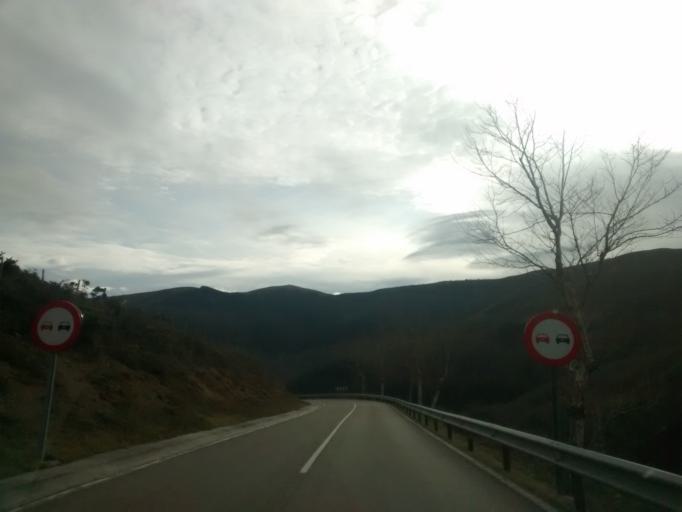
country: ES
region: Cantabria
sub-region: Provincia de Cantabria
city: Ruente
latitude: 43.2370
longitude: -4.3233
